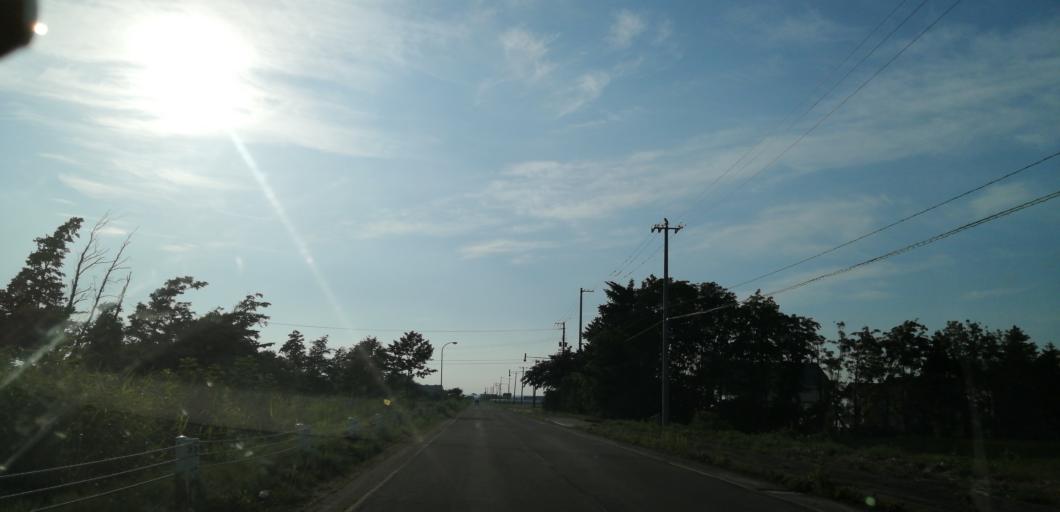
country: JP
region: Hokkaido
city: Kitahiroshima
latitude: 42.9507
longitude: 141.6693
